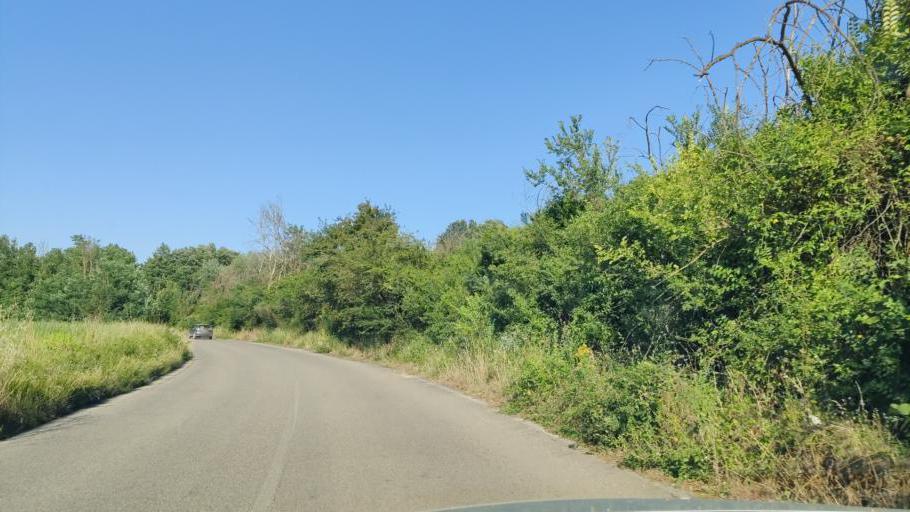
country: IT
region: Umbria
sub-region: Provincia di Terni
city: Penna in Teverina
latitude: 42.4783
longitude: 12.3705
